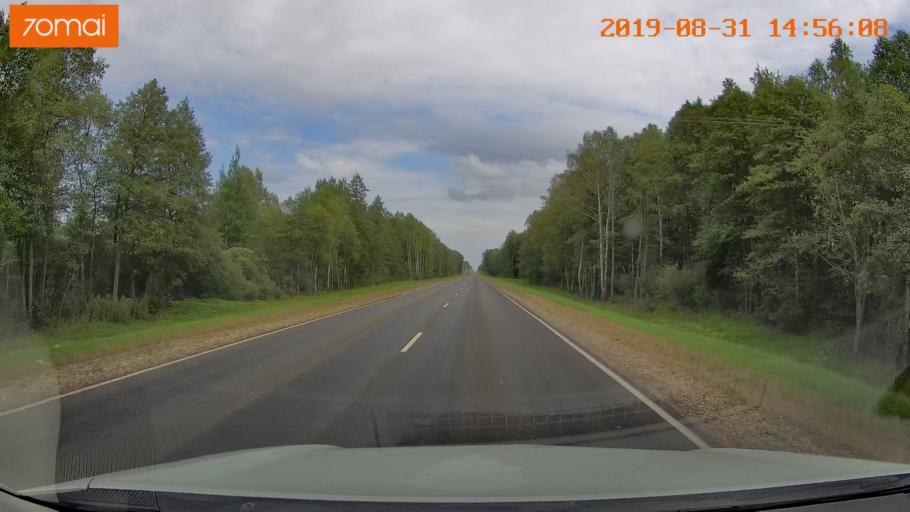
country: RU
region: Kaluga
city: Spas-Demensk
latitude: 54.3029
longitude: 33.9314
